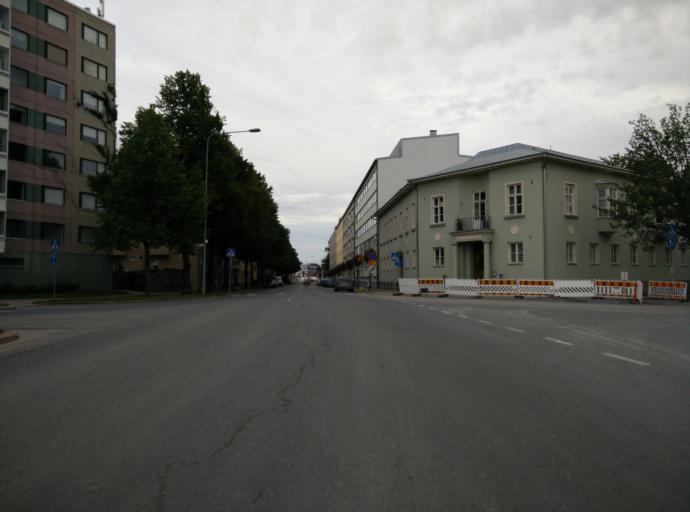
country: FI
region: Haeme
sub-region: Haemeenlinna
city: Haemeenlinna
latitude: 61.0018
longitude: 24.4768
